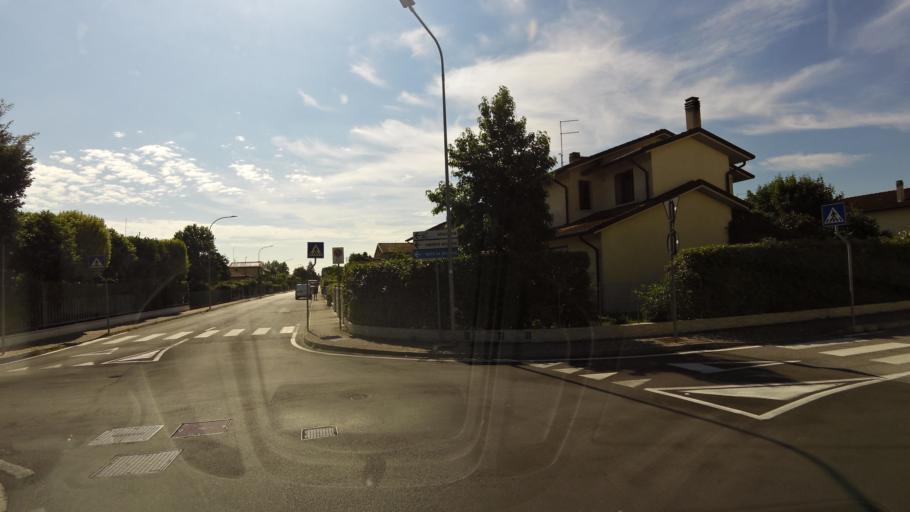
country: IT
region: Veneto
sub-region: Provincia di Venezia
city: Quarto d'Altino
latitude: 45.5762
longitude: 12.3622
